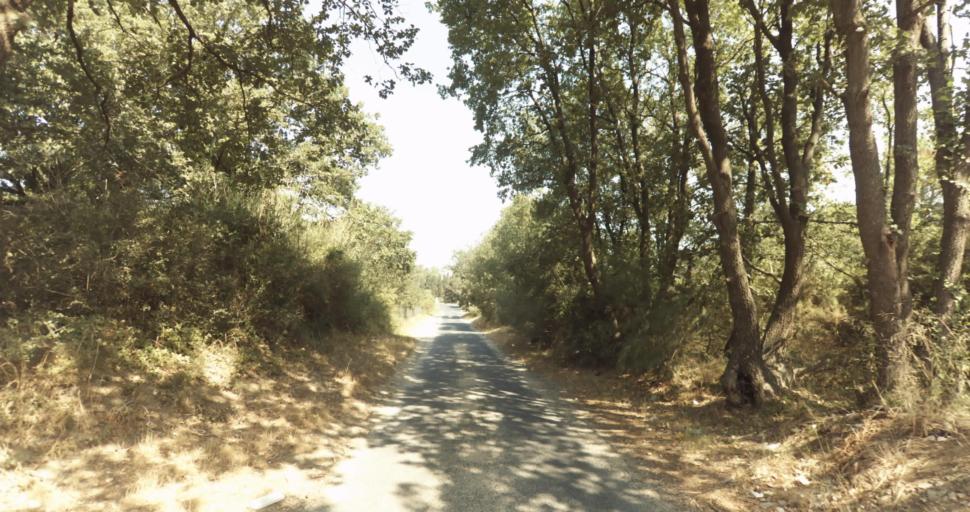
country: FR
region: Languedoc-Roussillon
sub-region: Departement des Pyrenees-Orientales
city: Latour-Bas-Elne
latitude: 42.6127
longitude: 2.9897
